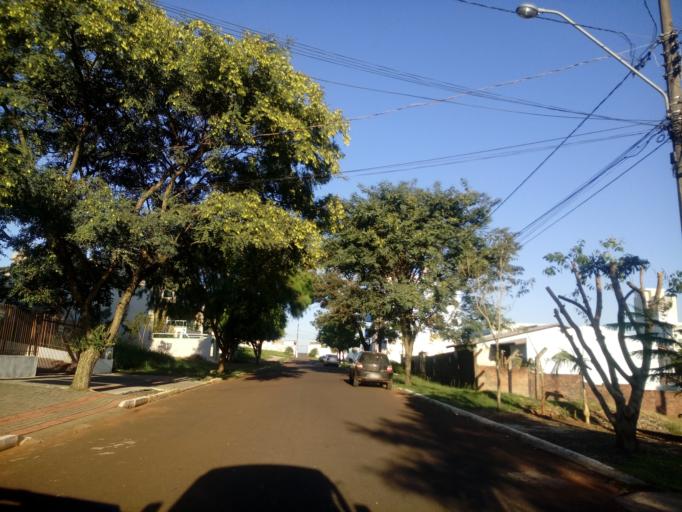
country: BR
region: Santa Catarina
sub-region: Chapeco
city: Chapeco
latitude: -27.1120
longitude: -52.6111
